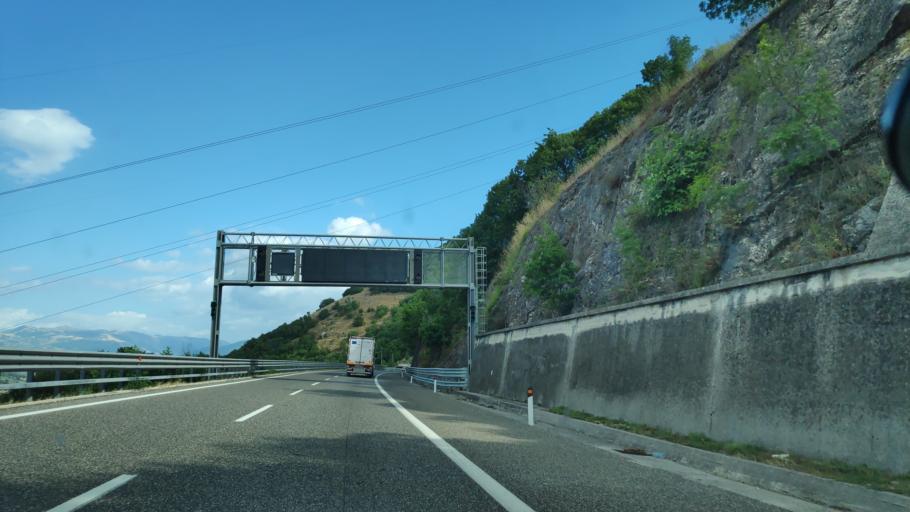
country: IT
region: Campania
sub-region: Provincia di Salerno
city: Sicignano degli Alburni
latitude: 40.5853
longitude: 15.3392
